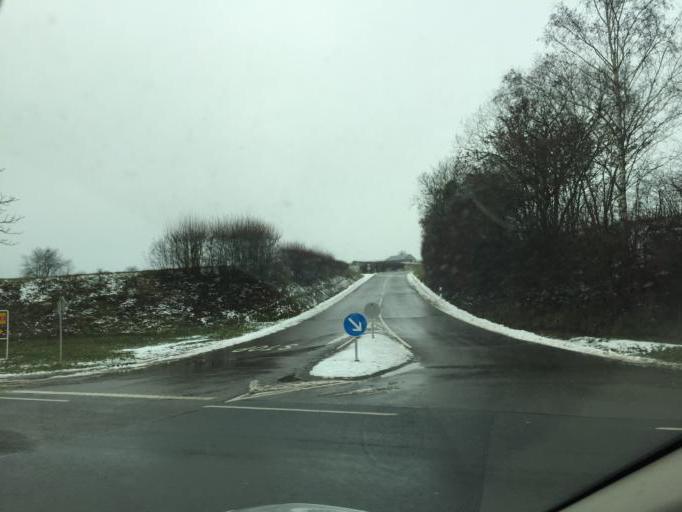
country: LU
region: Diekirch
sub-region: Canton de Diekirch
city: Niederfeulen
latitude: 49.8461
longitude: 6.0284
